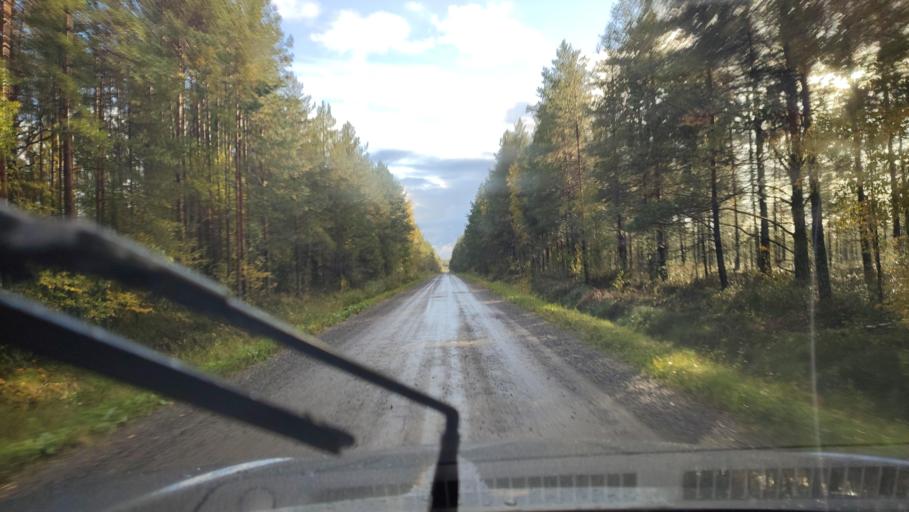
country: FI
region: Southern Ostrobothnia
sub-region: Suupohja
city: Karijoki
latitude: 62.3195
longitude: 21.5636
